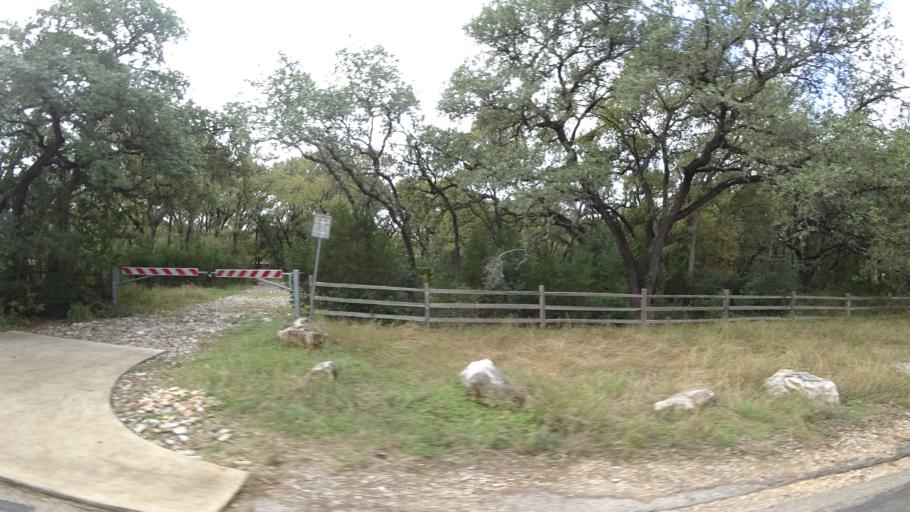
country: US
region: Texas
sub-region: Travis County
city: Shady Hollow
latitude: 30.2083
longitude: -97.8313
